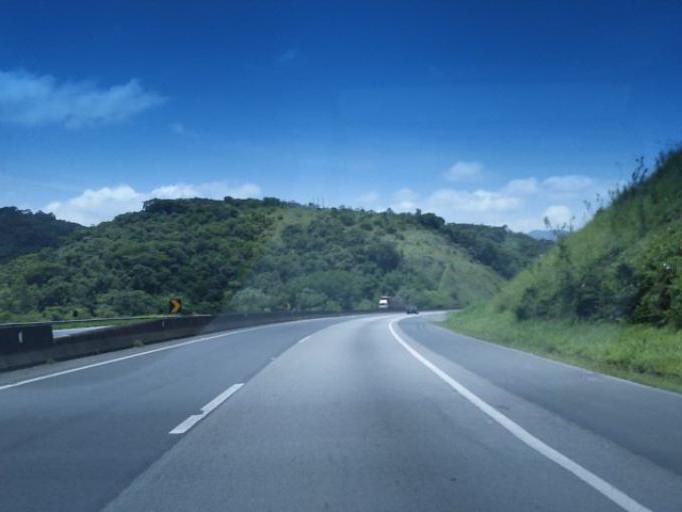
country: BR
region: Sao Paulo
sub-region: Miracatu
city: Miracatu
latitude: -24.2303
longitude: -47.3610
